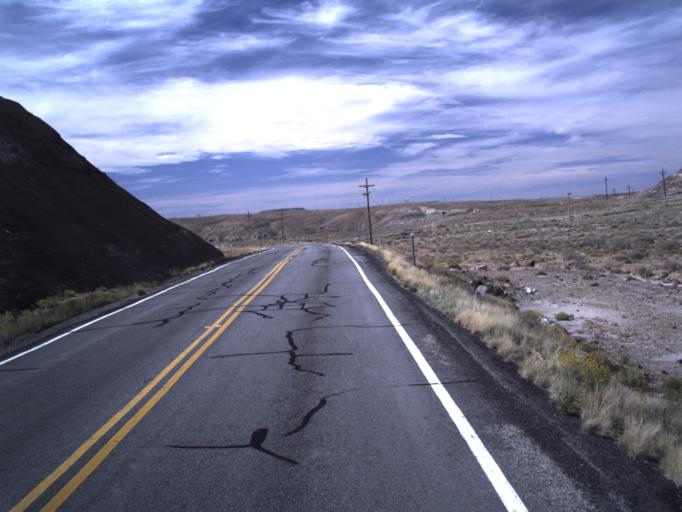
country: US
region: Utah
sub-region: San Juan County
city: Blanding
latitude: 37.3268
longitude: -109.3185
